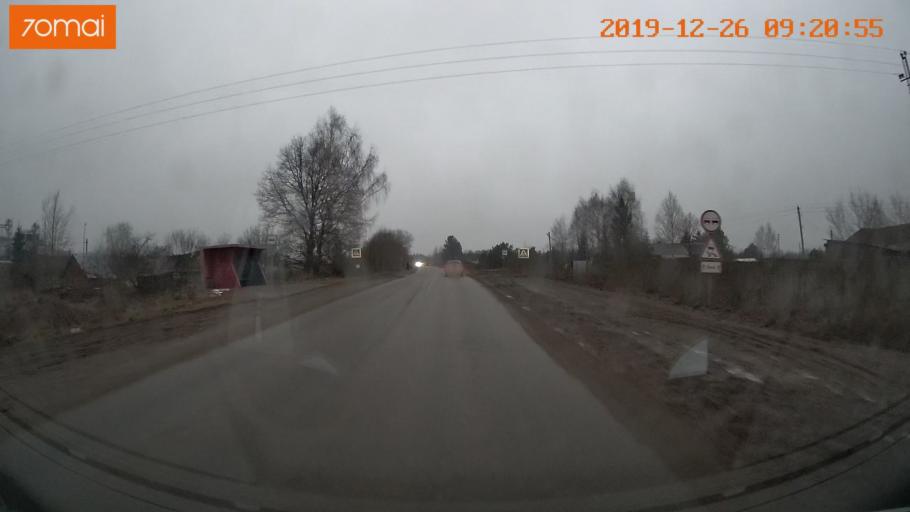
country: RU
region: Vologda
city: Gryazovets
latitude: 58.9657
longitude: 40.2271
